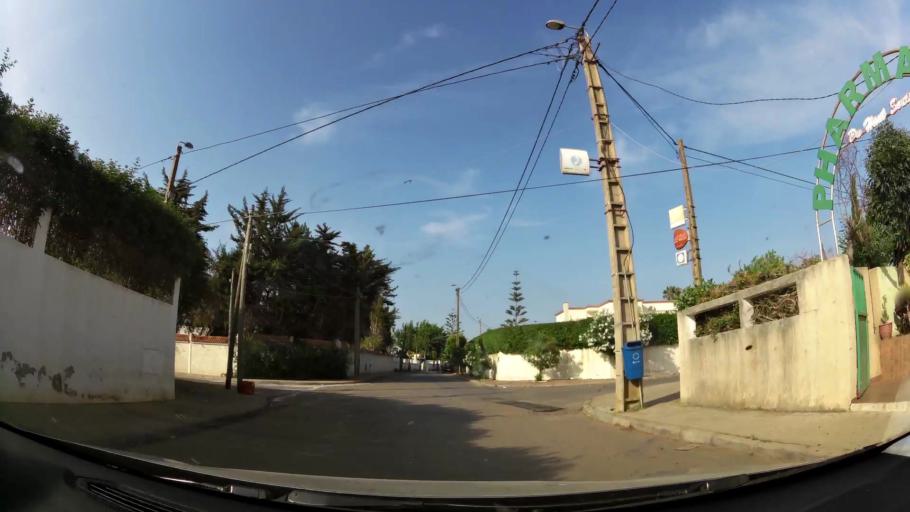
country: MA
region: Rabat-Sale-Zemmour-Zaer
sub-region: Rabat
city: Rabat
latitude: 33.9377
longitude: -6.8142
